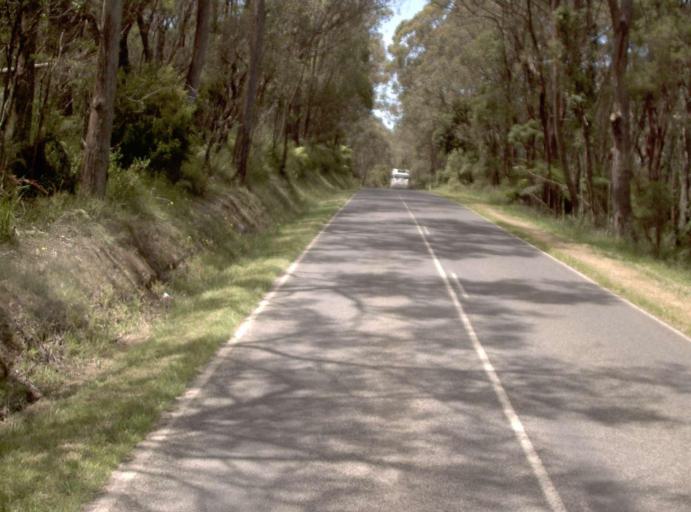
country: AU
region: Victoria
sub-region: Bass Coast
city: North Wonthaggi
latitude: -38.7322
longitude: 146.1244
